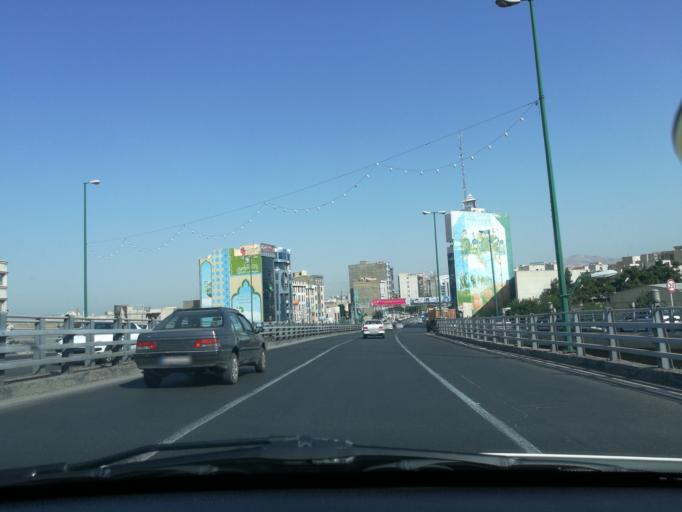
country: IR
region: Alborz
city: Karaj
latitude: 35.8316
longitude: 50.9981
